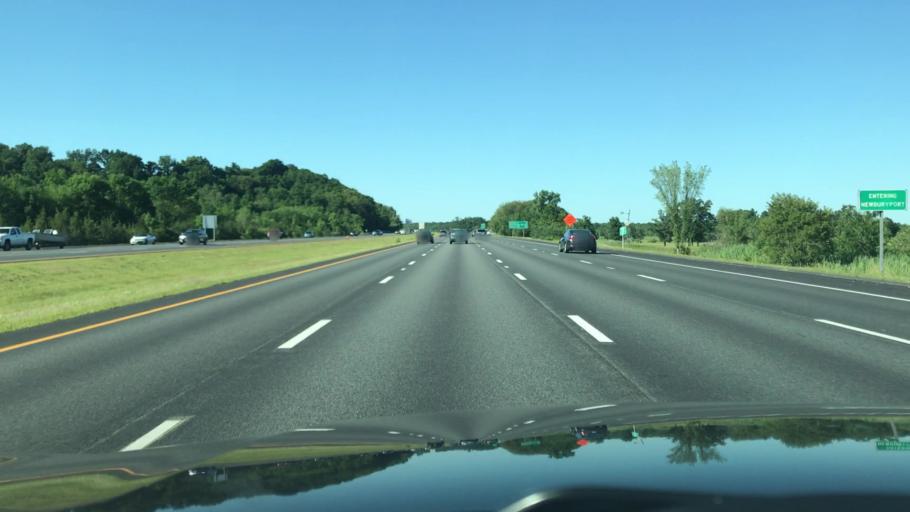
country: US
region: Massachusetts
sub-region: Essex County
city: Newburyport
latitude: 42.7906
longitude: -70.9203
